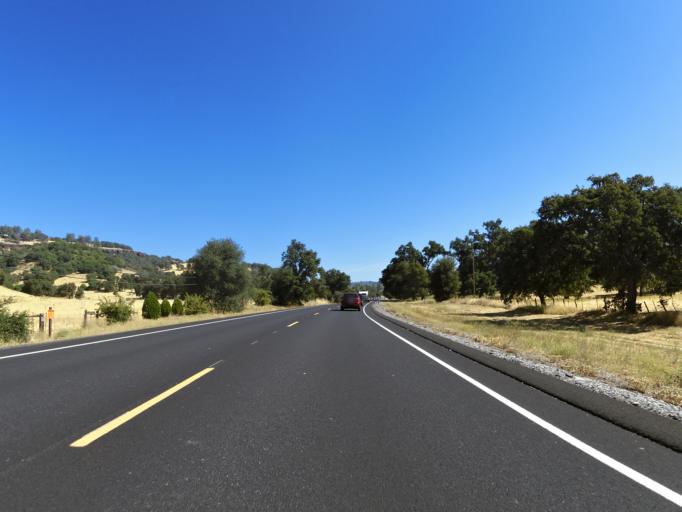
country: US
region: California
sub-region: Calaveras County
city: Murphys
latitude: 38.1023
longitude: -120.4688
